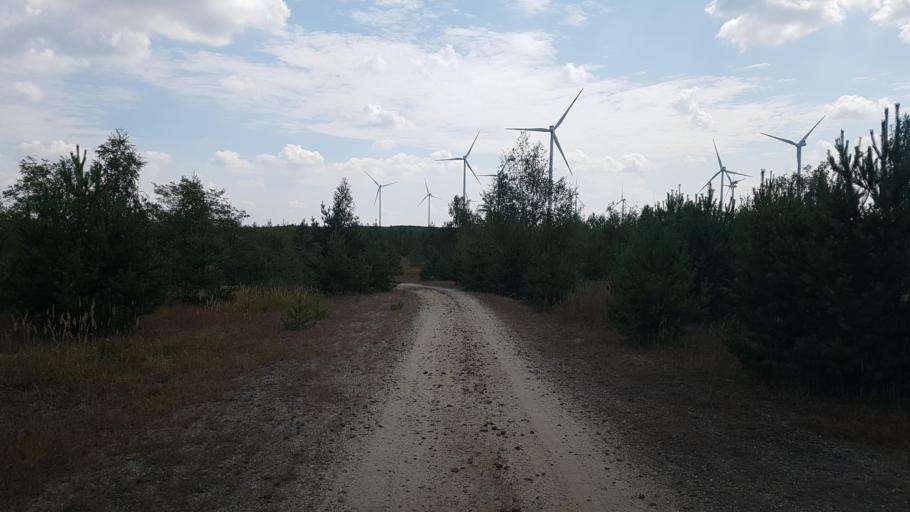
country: DE
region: Brandenburg
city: Sallgast
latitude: 51.5617
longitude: 13.8475
